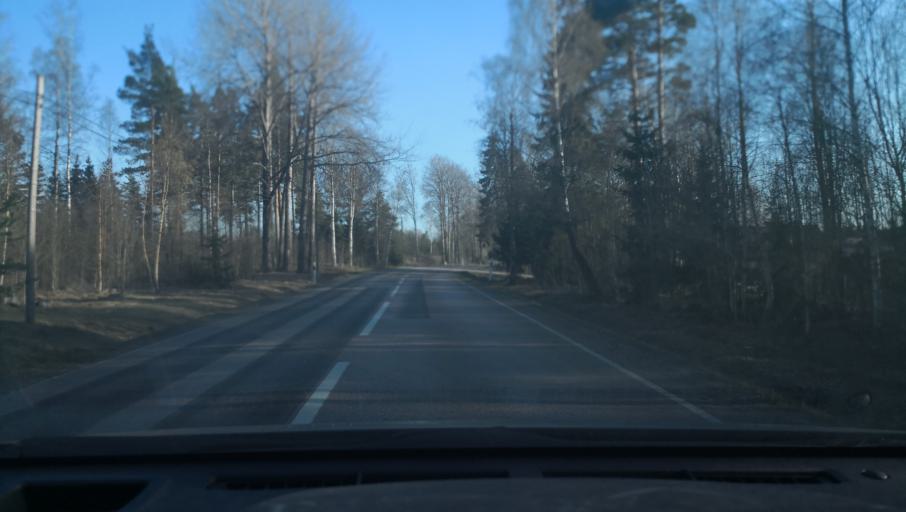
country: SE
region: Uppsala
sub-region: Heby Kommun
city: Heby
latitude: 59.9877
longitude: 16.8326
